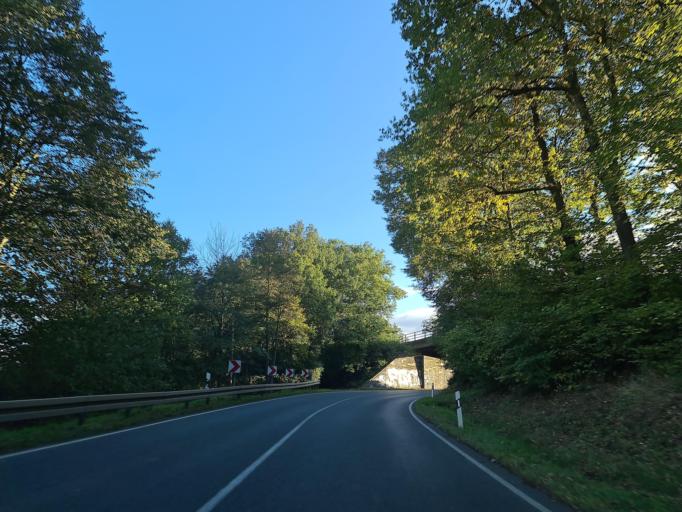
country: DE
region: Thuringia
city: Wunschendorf
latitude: 50.8099
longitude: 12.0760
